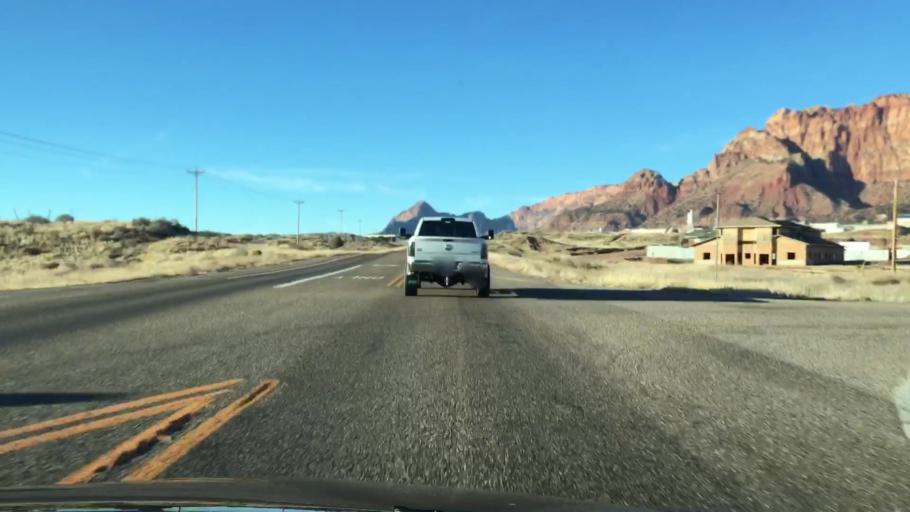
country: US
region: Arizona
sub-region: Mohave County
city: Colorado City
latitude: 36.9909
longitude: -112.9910
